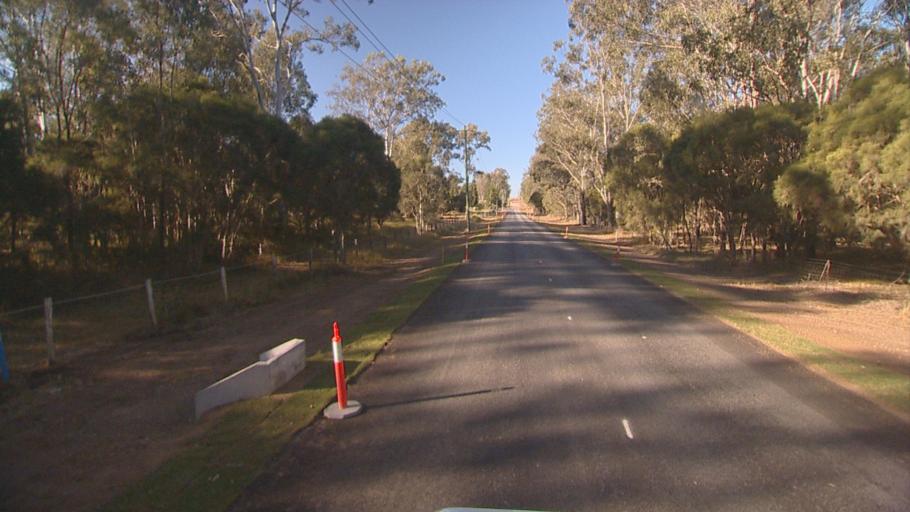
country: AU
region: Queensland
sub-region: Logan
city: Cedar Vale
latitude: -27.8343
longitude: 152.9983
